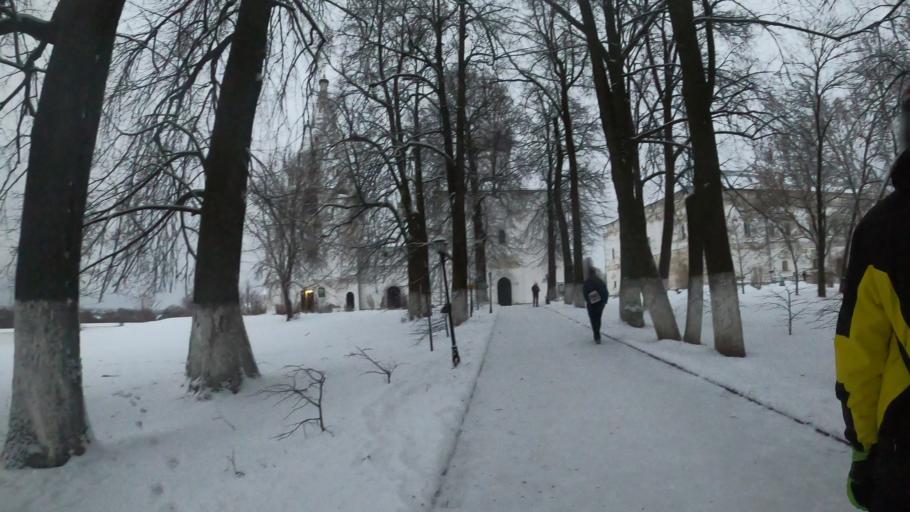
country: RU
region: Jaroslavl
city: Pereslavl'-Zalesskiy
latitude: 56.7205
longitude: 38.8376
